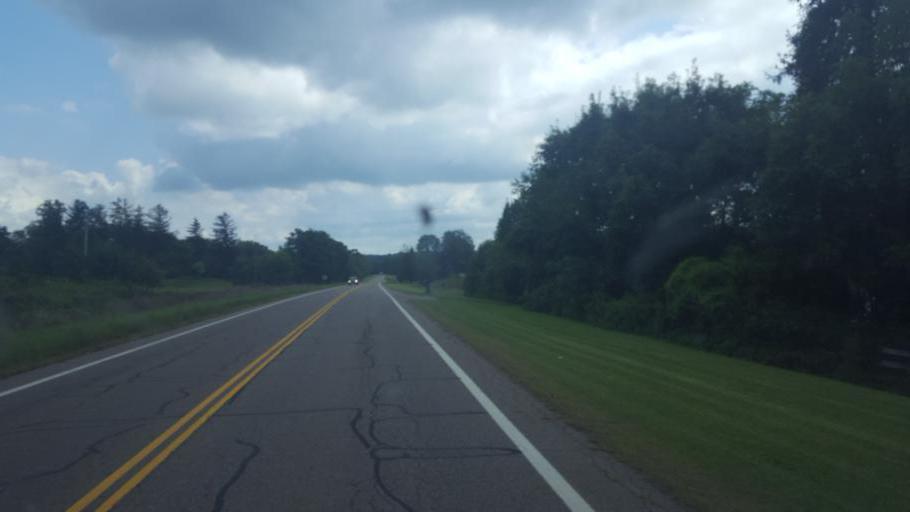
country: US
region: Ohio
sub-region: Knox County
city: Gambier
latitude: 40.3686
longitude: -82.3974
